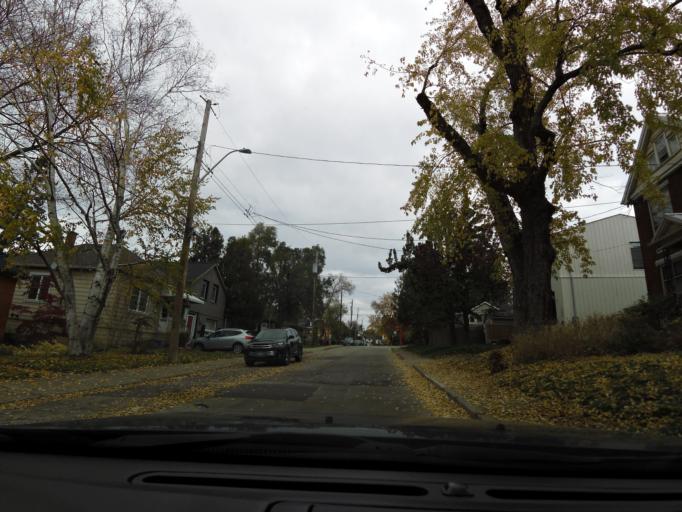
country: CA
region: Ontario
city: Hamilton
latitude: 43.2660
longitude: -79.8881
